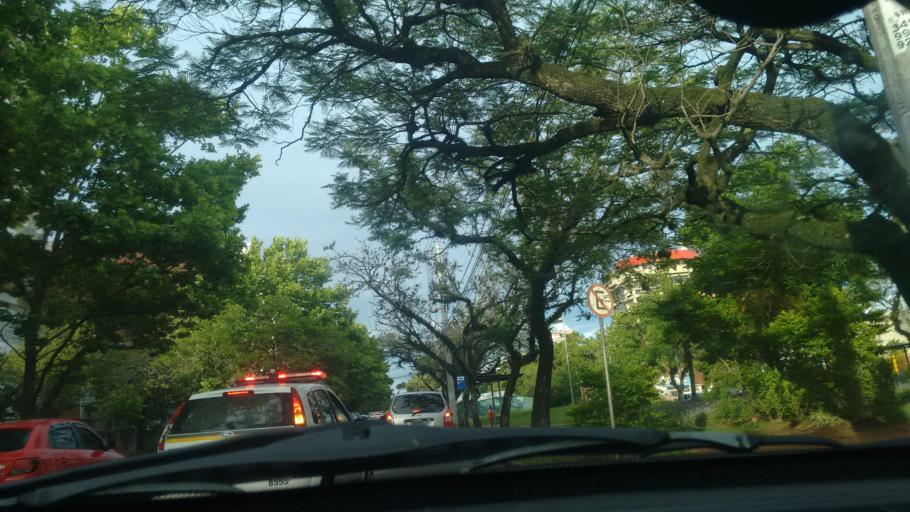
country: BR
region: Rio Grande do Sul
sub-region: Porto Alegre
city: Porto Alegre
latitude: -30.0209
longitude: -51.1817
